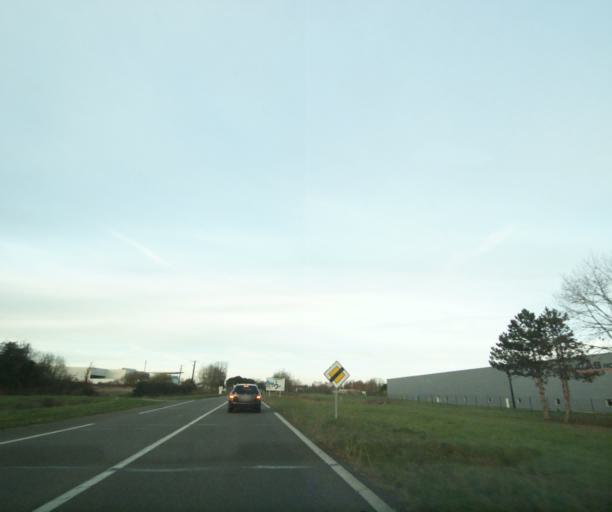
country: FR
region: Aquitaine
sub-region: Departement de la Gironde
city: Bazas
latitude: 44.4411
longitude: -0.2375
